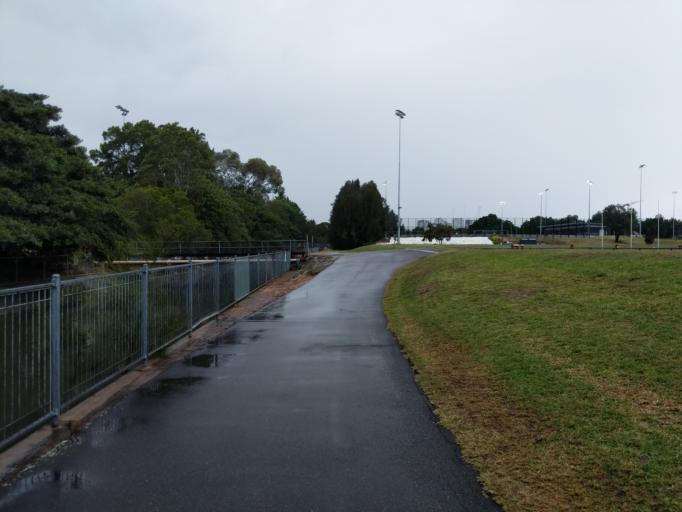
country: AU
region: New South Wales
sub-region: Ashfield
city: Croydon
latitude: -33.8647
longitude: 151.1120
